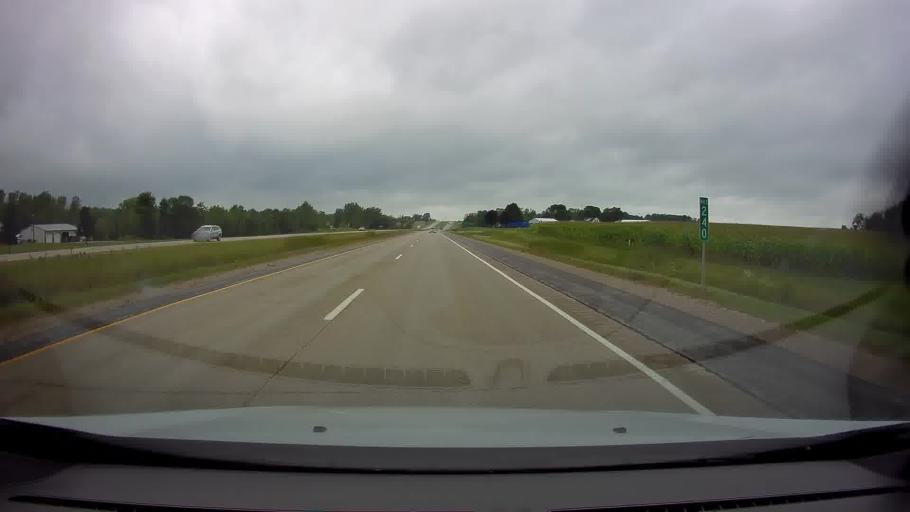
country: US
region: Wisconsin
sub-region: Brown County
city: Pulaski
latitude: 44.6943
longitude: -88.3419
